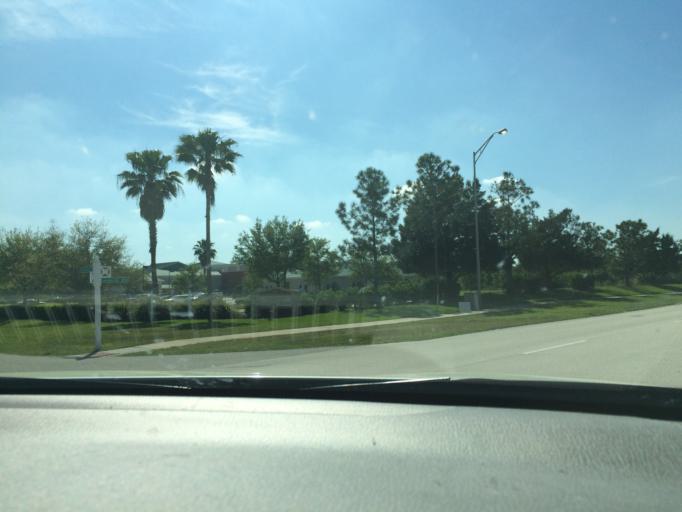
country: US
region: Florida
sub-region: Sarasota County
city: The Meadows
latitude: 27.3914
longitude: -82.3983
